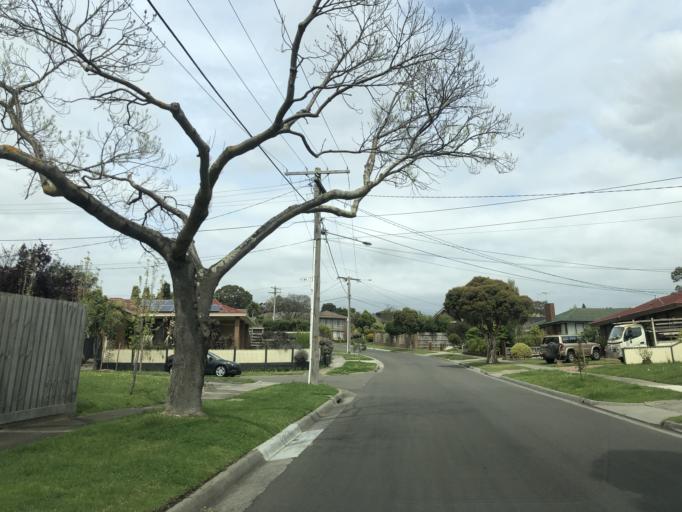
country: AU
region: Victoria
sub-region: Greater Dandenong
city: Noble Park North
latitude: -37.9407
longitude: 145.2115
